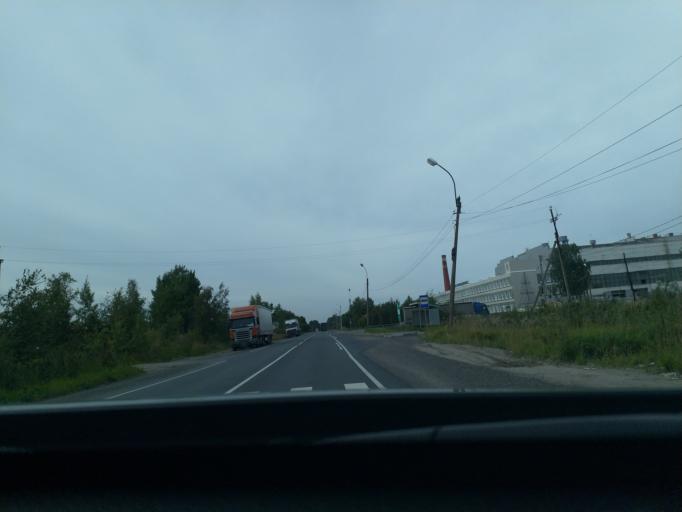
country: RU
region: Leningrad
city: Nikol'skoye
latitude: 59.7265
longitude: 30.7778
